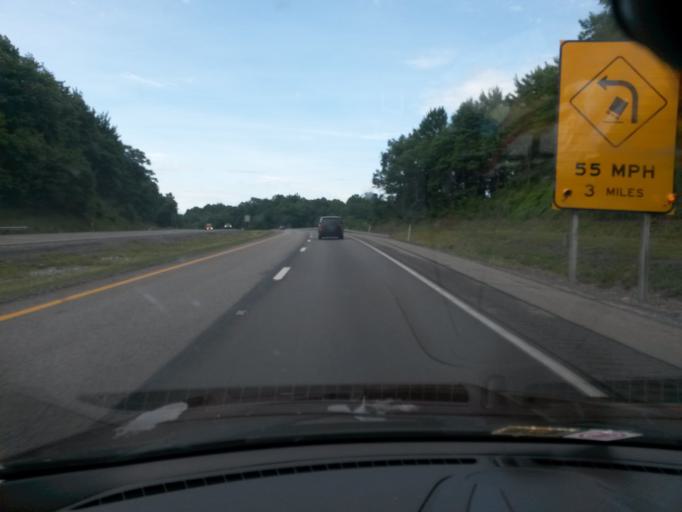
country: US
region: West Virginia
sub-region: Mercer County
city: Athens
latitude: 37.5444
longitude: -81.1159
